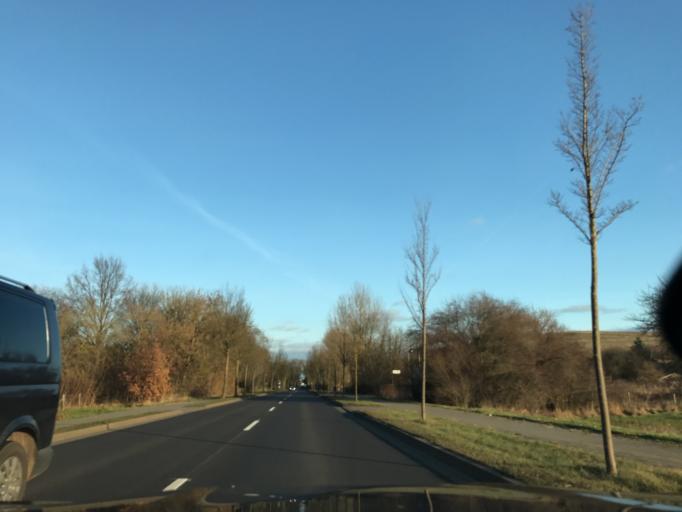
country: DE
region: Saxony-Anhalt
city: Burg bei Magdeburg
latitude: 52.2752
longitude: 11.8877
